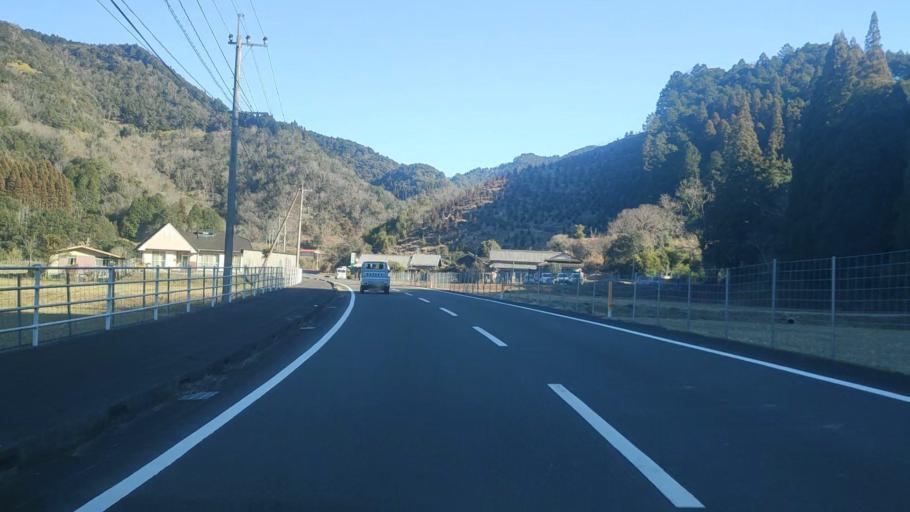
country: JP
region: Oita
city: Saiki
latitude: 32.7711
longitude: 131.8134
